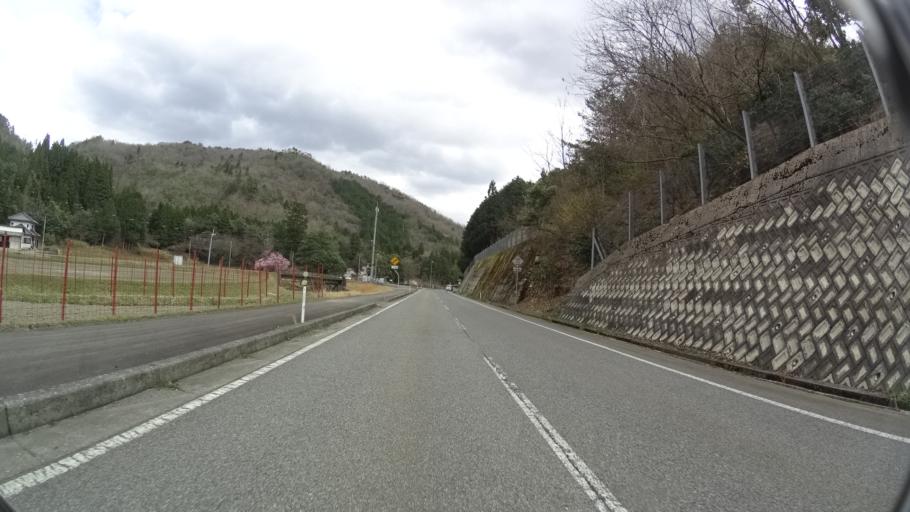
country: JP
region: Hyogo
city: Toyooka
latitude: 35.4831
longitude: 134.9251
